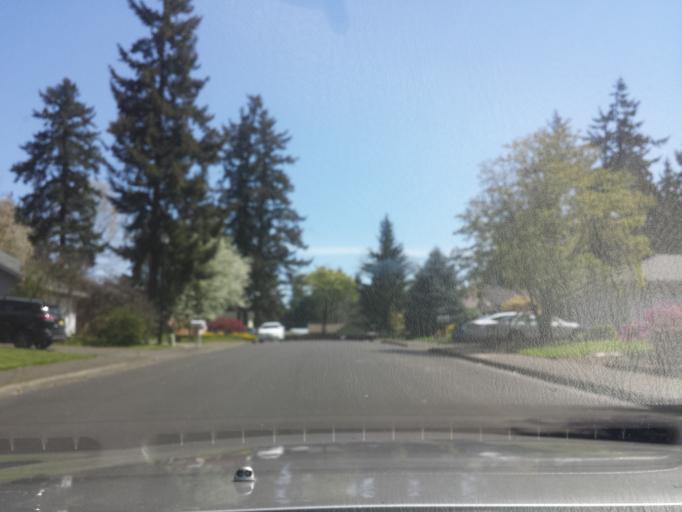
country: US
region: Oregon
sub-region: Washington County
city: Aloha
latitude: 45.4836
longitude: -122.8598
